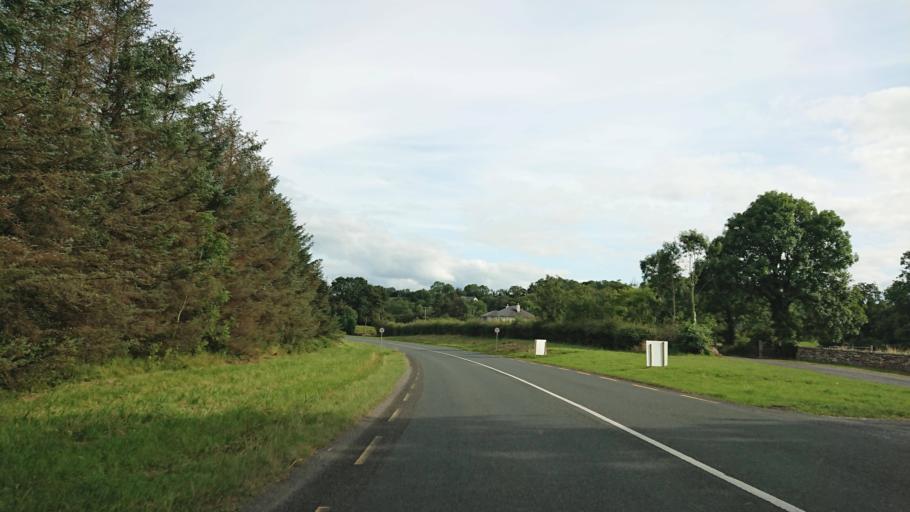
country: IE
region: Connaught
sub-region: County Leitrim
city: Carrick-on-Shannon
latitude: 53.9811
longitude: -8.0653
